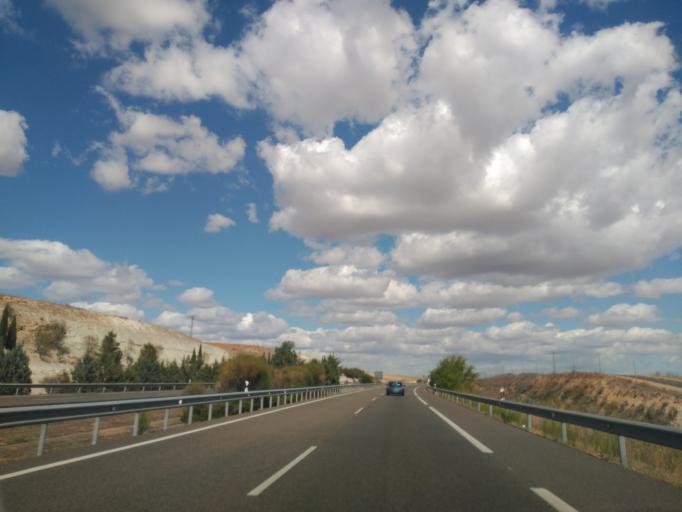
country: ES
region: Castille and Leon
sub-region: Provincia de Palencia
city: Venta de Banos
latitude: 41.9416
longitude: -4.4855
